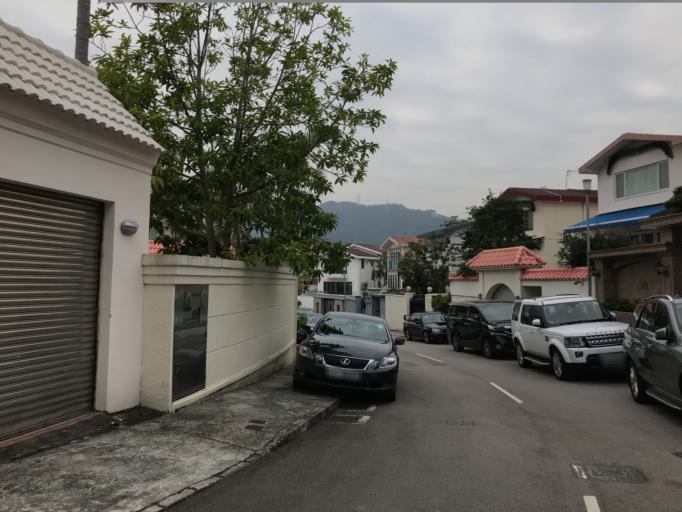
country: HK
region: Tai Po
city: Tai Po
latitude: 22.4641
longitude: 114.1571
